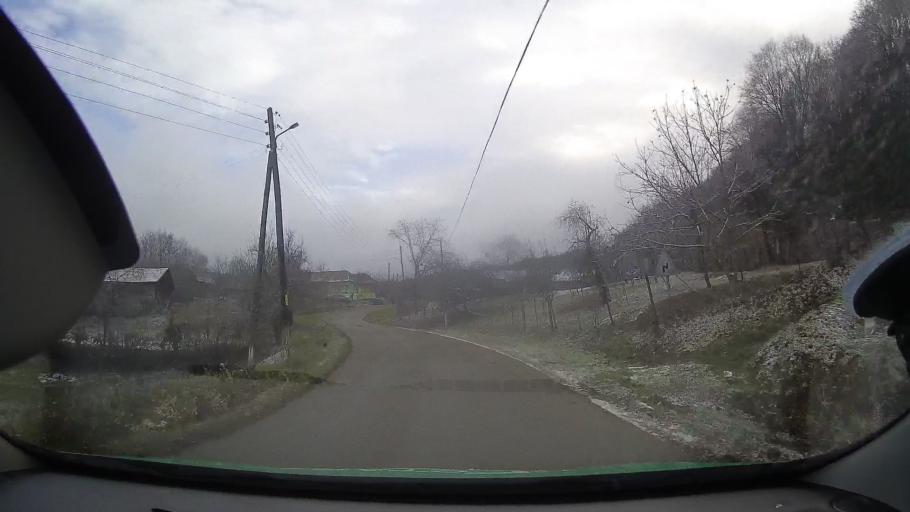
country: RO
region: Mures
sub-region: Comuna Chetani
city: Chetani
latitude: 46.4048
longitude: 24.0124
